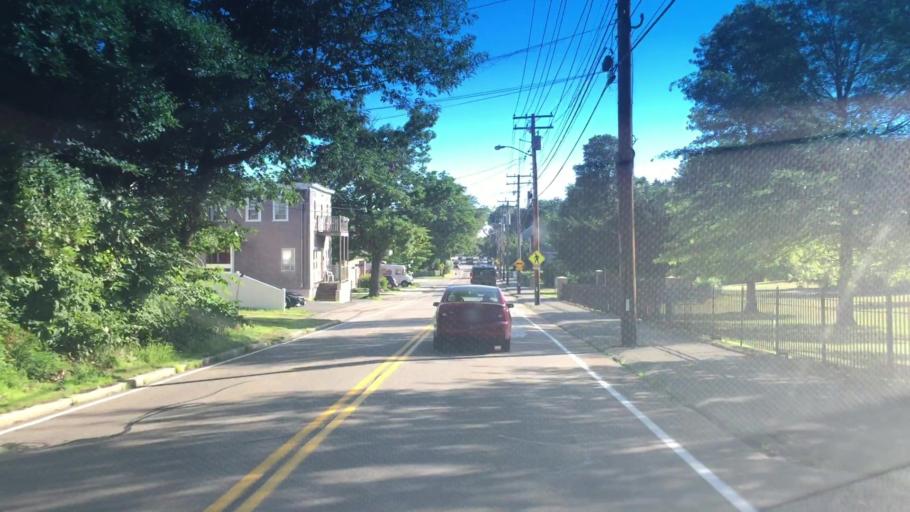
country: US
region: Massachusetts
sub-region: Norfolk County
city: Walpole
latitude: 42.1578
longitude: -71.2195
